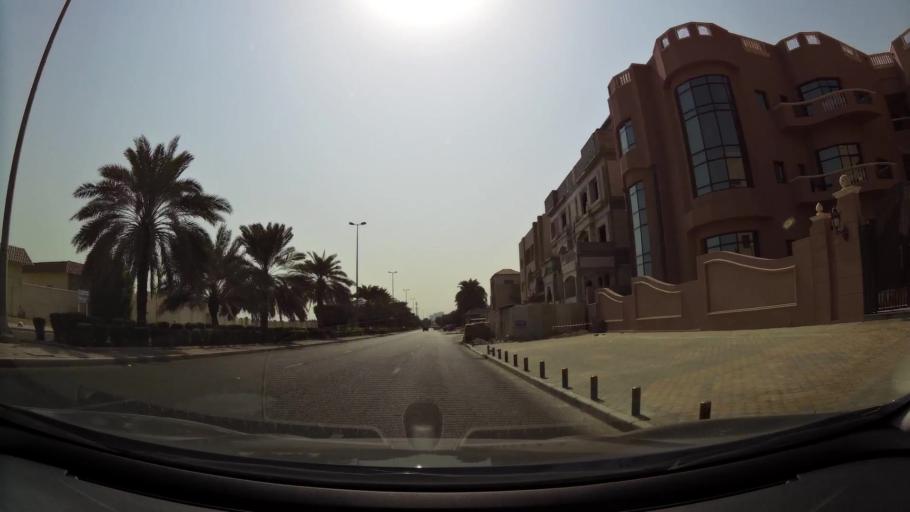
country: KW
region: Al Ahmadi
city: Al Fintas
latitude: 29.1757
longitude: 48.1223
